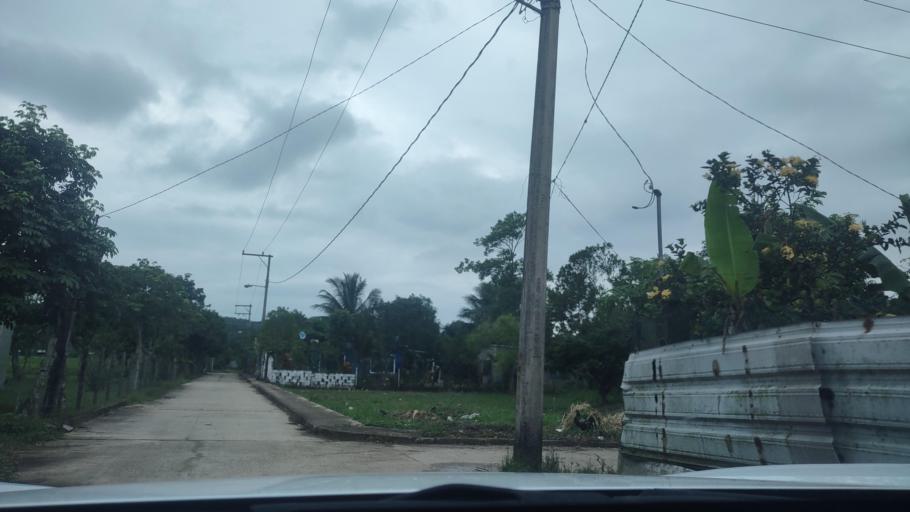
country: MX
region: Veracruz
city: Villa Nanchital
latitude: 18.0416
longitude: -94.3506
